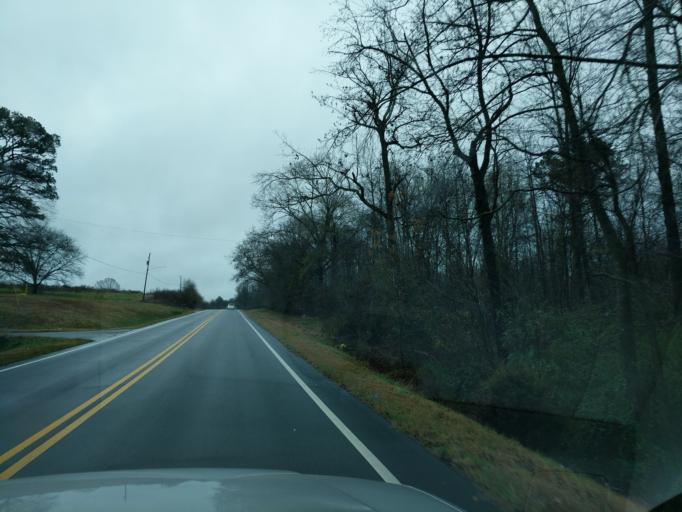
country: US
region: Georgia
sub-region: Franklin County
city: Lavonia
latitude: 34.3826
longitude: -83.0923
